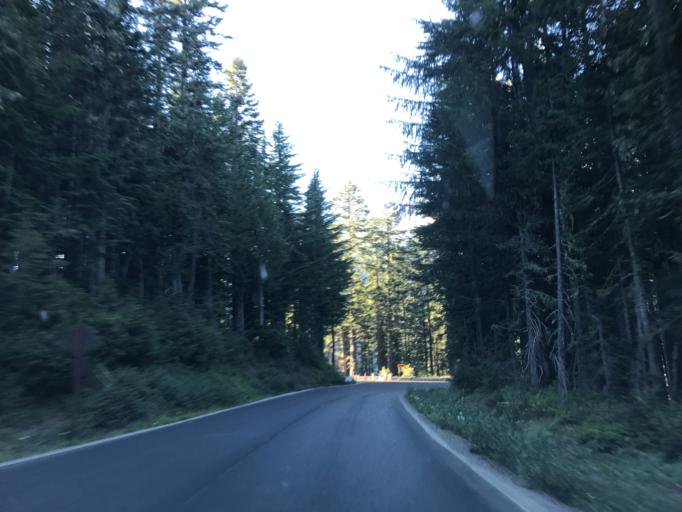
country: US
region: Washington
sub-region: Pierce County
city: Buckley
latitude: 46.7712
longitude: -121.7764
